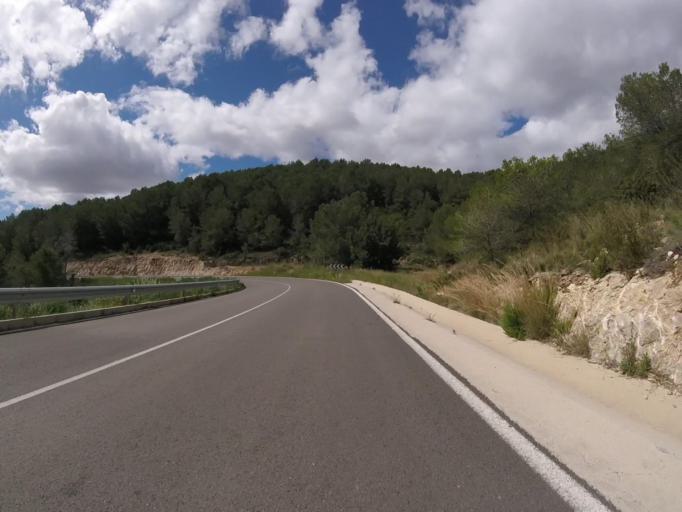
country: ES
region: Valencia
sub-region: Provincia de Castello
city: Adzaneta
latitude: 40.2717
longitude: -0.1104
